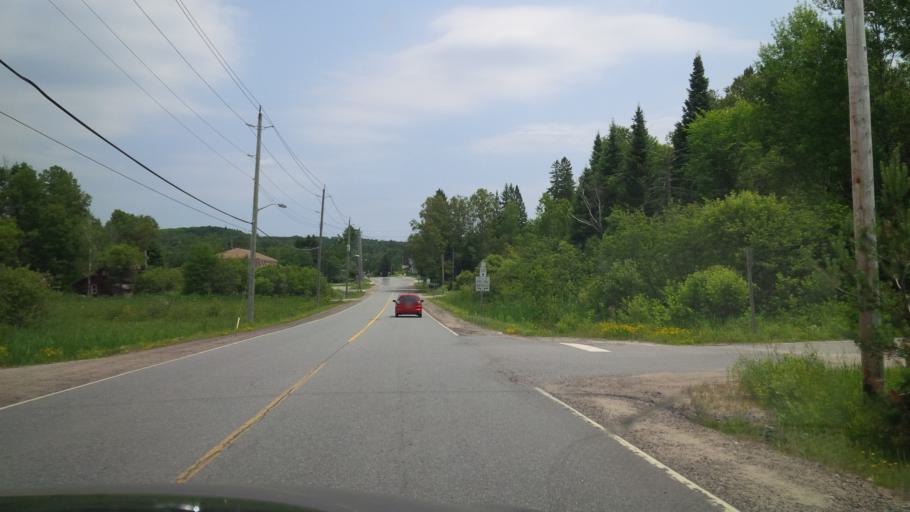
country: CA
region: Ontario
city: Huntsville
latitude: 45.5283
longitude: -79.3197
